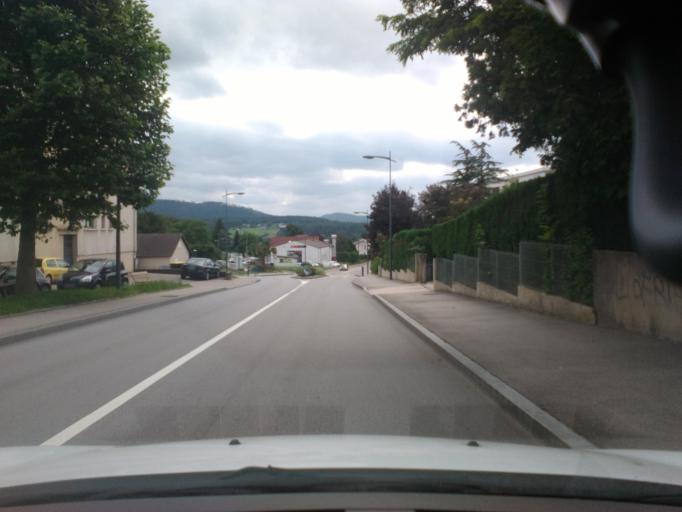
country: FR
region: Lorraine
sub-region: Departement des Vosges
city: Bruyeres
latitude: 48.2015
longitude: 6.7119
